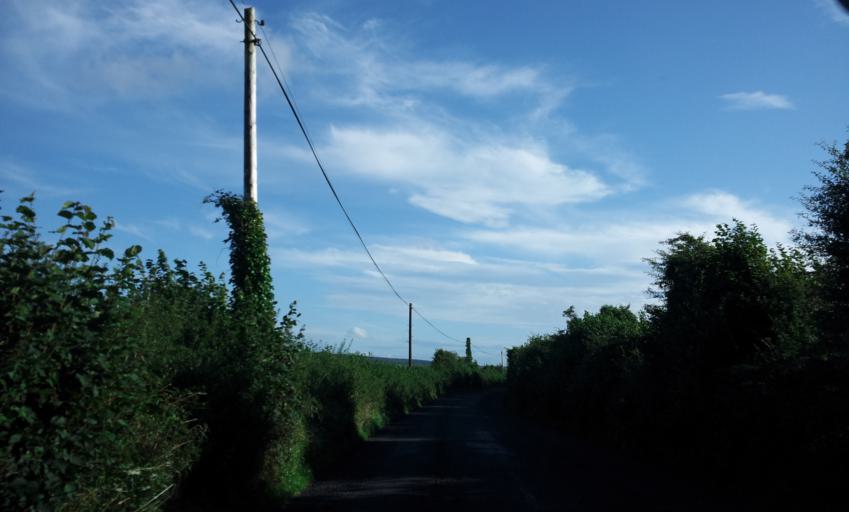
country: IE
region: Munster
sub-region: An Clar
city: Ennis
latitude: 53.0015
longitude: -9.1281
